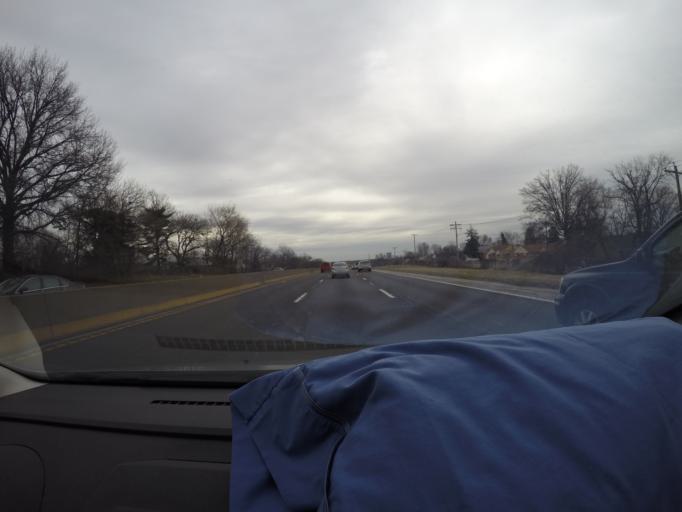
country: US
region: Missouri
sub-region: Saint Louis County
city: Northwoods
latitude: 38.7081
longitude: -90.2774
